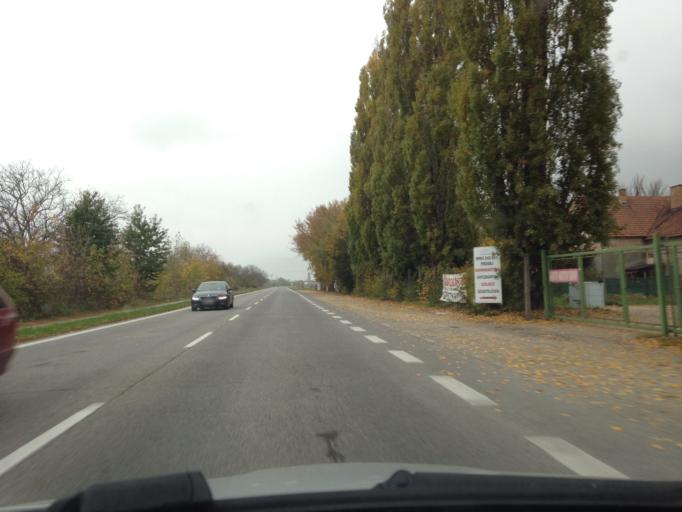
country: SK
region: Nitriansky
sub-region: Okres Nove Zamky
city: Sturovo
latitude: 47.7930
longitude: 18.6959
